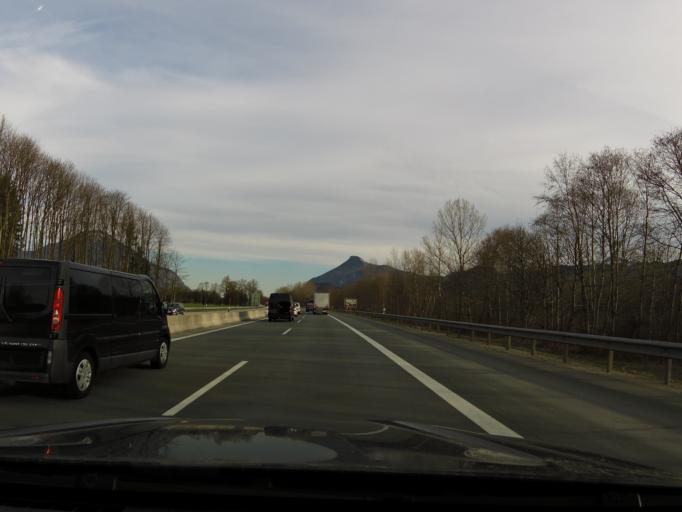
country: DE
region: Bavaria
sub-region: Upper Bavaria
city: Kiefersfelden
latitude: 47.6263
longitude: 12.2013
